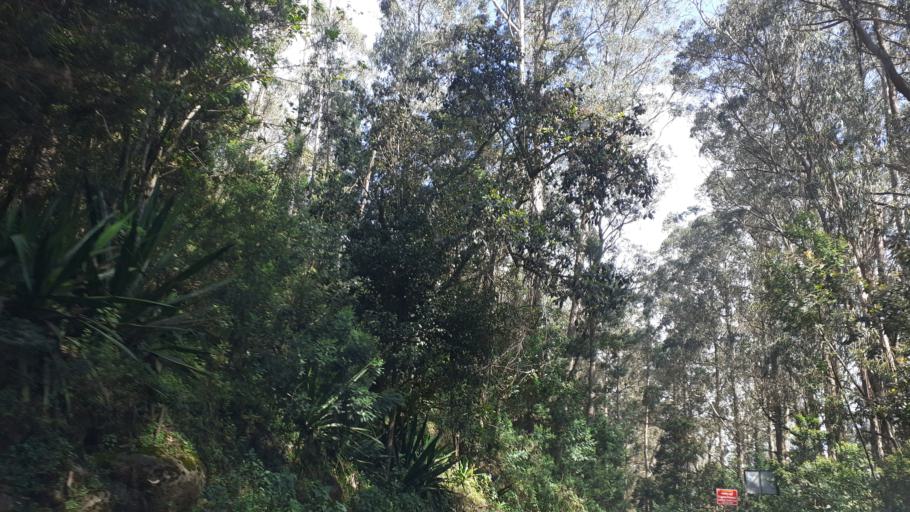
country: IN
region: Tamil Nadu
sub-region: Dindigul
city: Kodaikanal
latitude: 10.2283
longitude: 77.4234
